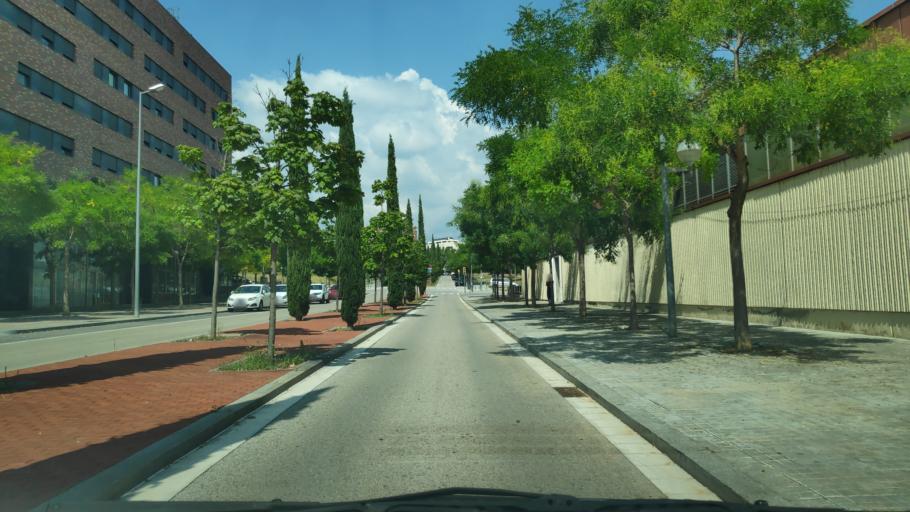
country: ES
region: Catalonia
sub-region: Provincia de Barcelona
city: Sant Quirze del Valles
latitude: 41.5469
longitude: 2.0841
